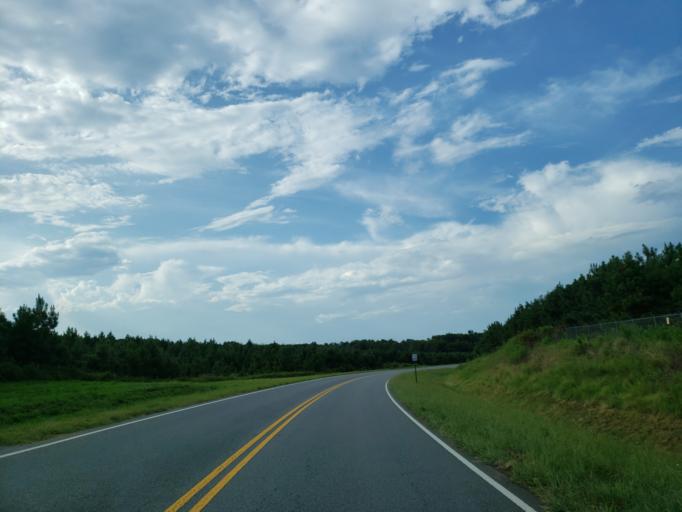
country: US
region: Georgia
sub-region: Bartow County
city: Euharlee
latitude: 34.1258
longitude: -84.9404
